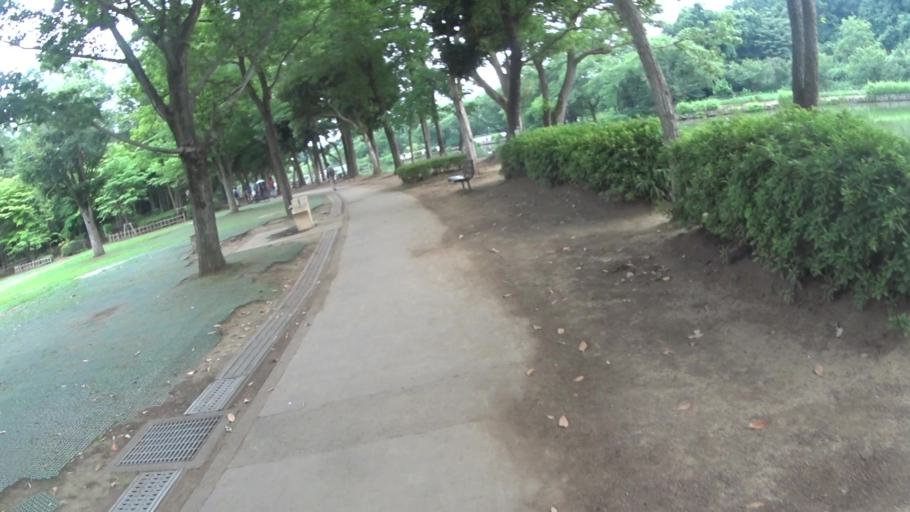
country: JP
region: Saitama
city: Okegawa
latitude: 35.9559
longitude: 139.5480
